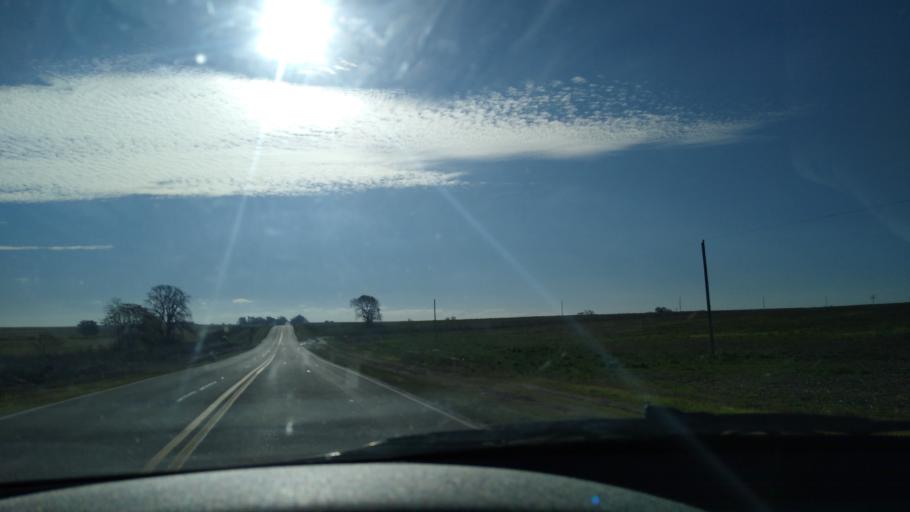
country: AR
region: Entre Rios
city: Aranguren
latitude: -32.3462
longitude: -60.3681
